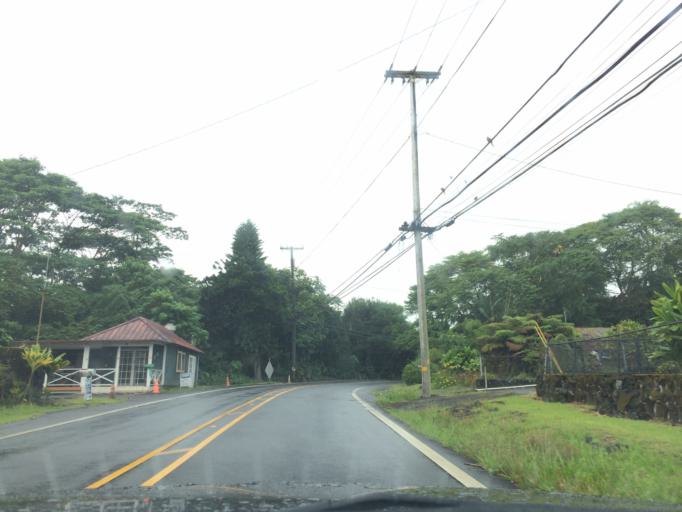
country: US
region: Hawaii
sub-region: Hawaii County
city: Hilo
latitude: 19.6948
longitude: -155.1202
